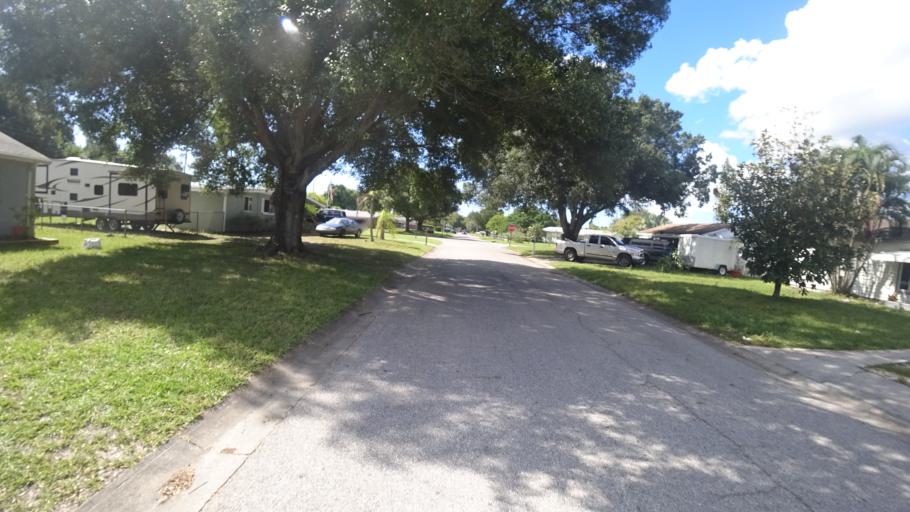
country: US
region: Florida
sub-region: Manatee County
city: South Bradenton
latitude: 27.4743
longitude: -82.5803
